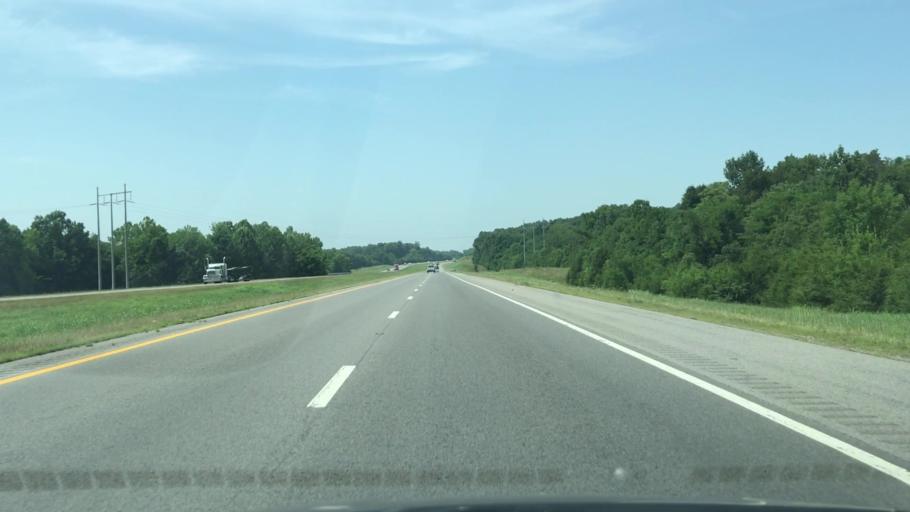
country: US
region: Tennessee
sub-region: Wilson County
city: Lebanon
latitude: 36.1610
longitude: -86.3586
